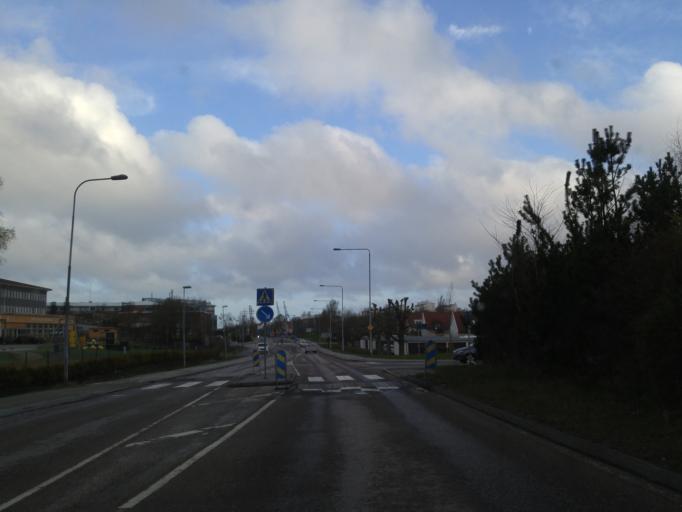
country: SE
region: Vaestra Goetaland
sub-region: Goteborg
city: Majorna
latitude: 57.6711
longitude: 11.8855
